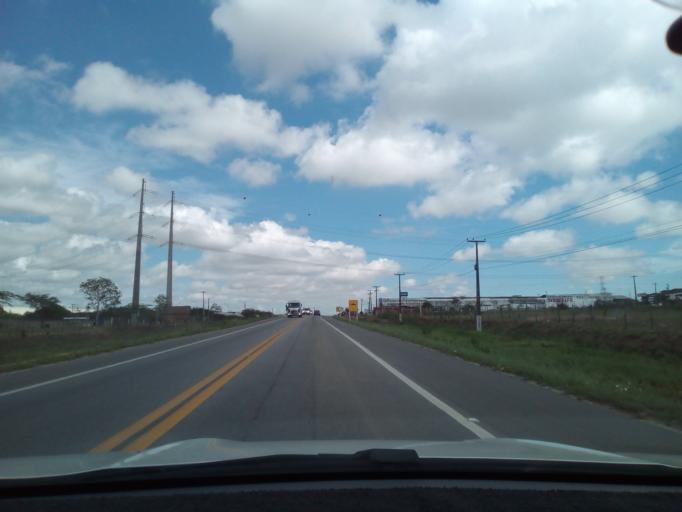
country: BR
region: Paraiba
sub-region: Campina Grande
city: Campina Grande
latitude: -7.2788
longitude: -35.8938
